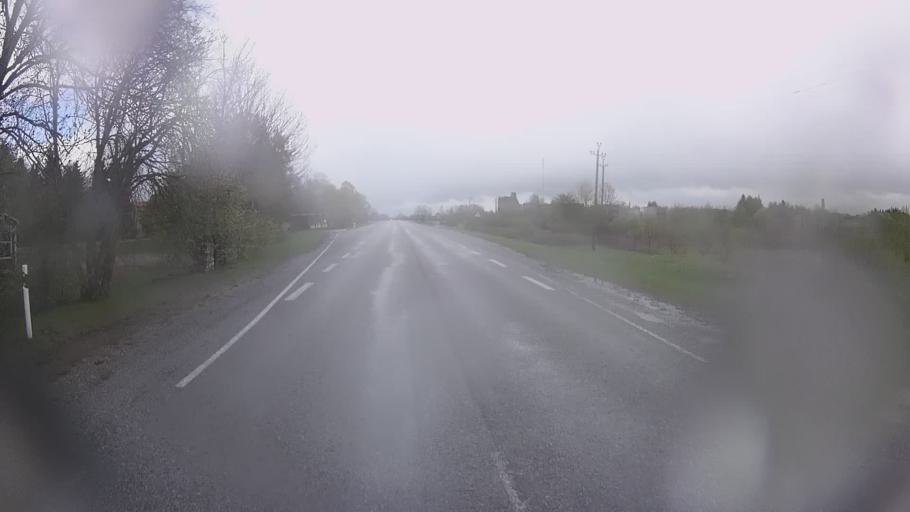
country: EE
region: Hiiumaa
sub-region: Kaerdla linn
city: Kardla
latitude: 58.8299
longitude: 22.7663
